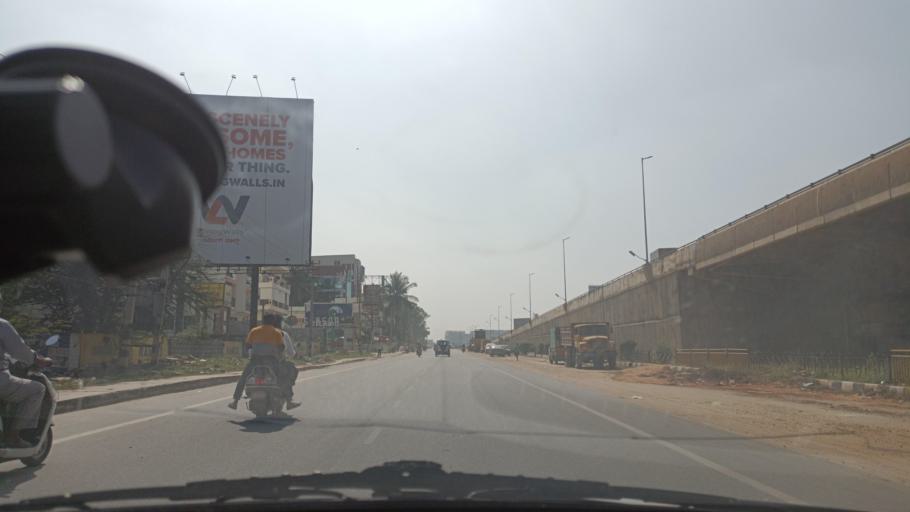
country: IN
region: Karnataka
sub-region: Bangalore Urban
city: Yelahanka
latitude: 13.1591
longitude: 77.6255
